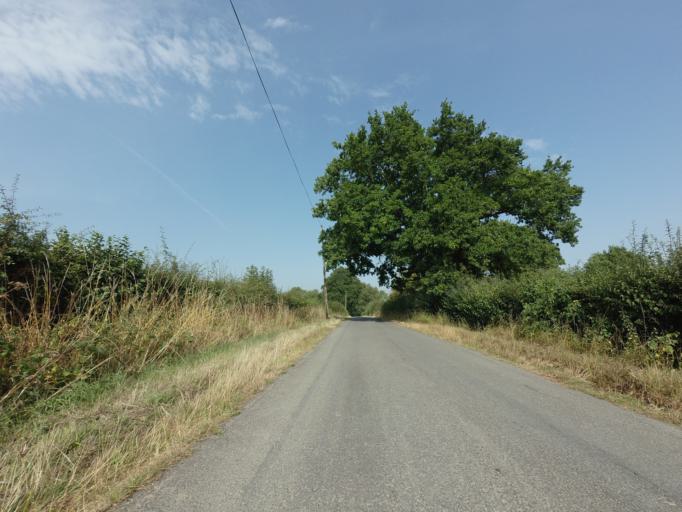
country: GB
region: England
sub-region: Kent
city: Headcorn
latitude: 51.1199
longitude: 0.6051
